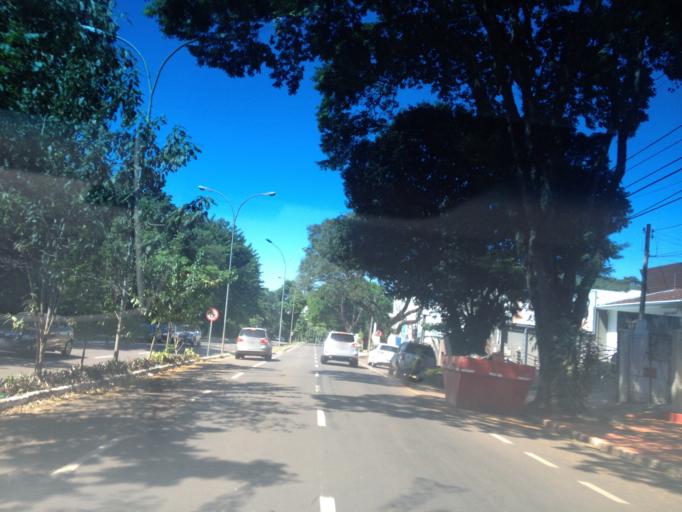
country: BR
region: Parana
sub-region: Maringa
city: Maringa
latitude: -23.4318
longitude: -51.9466
